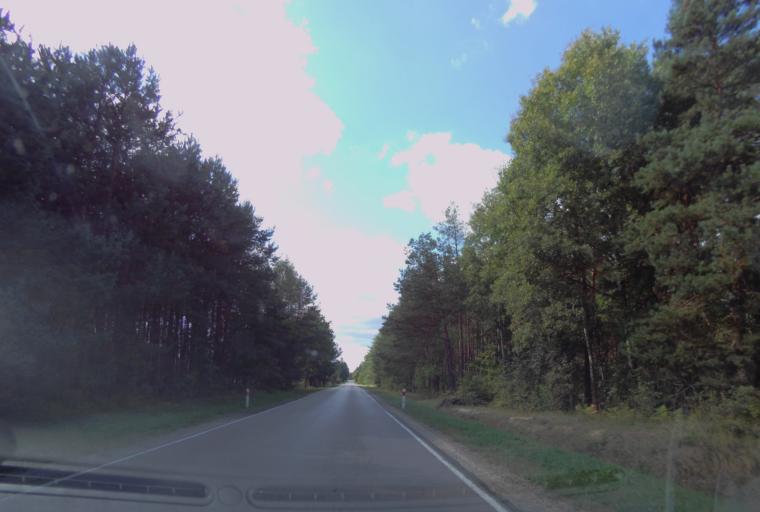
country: PL
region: Subcarpathian Voivodeship
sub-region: Powiat tarnobrzeski
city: Nowa Deba
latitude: 50.4104
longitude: 21.8294
